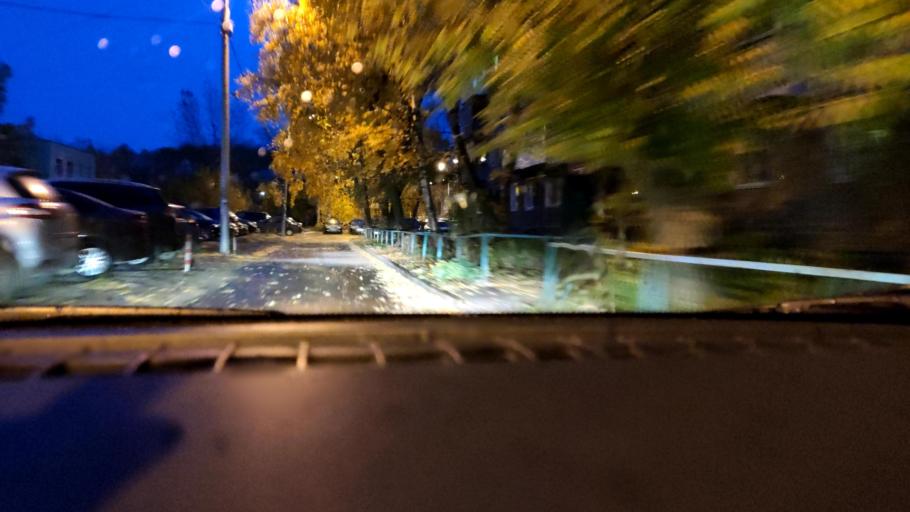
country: RU
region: Perm
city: Perm
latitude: 57.9668
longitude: 56.1942
